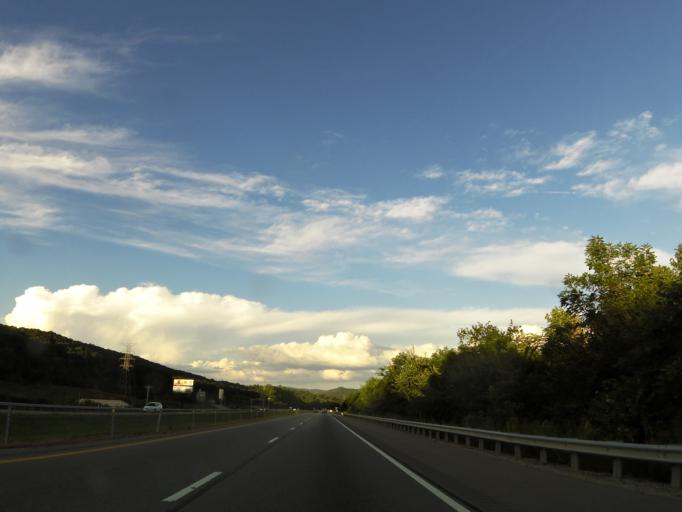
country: US
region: Tennessee
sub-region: Putnam County
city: Algood
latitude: 36.1390
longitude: -85.4441
